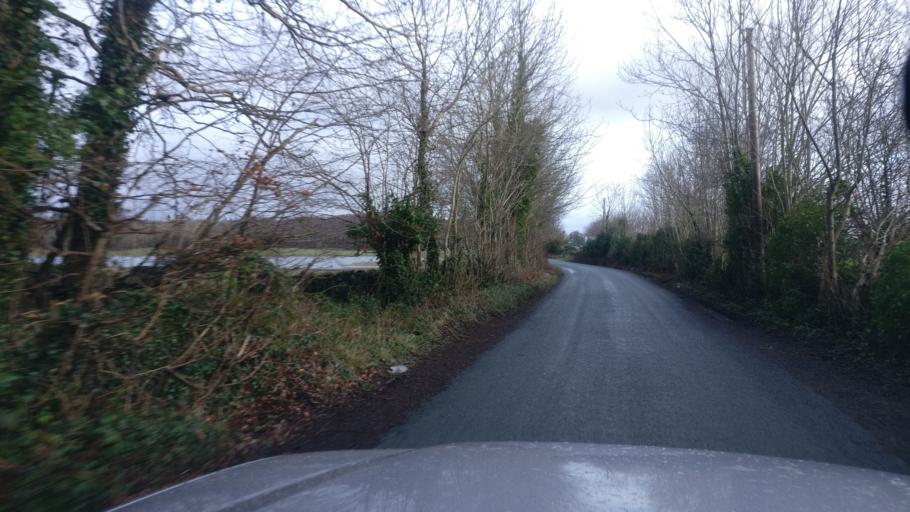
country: IE
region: Connaught
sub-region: County Galway
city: Athenry
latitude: 53.2575
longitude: -8.7140
